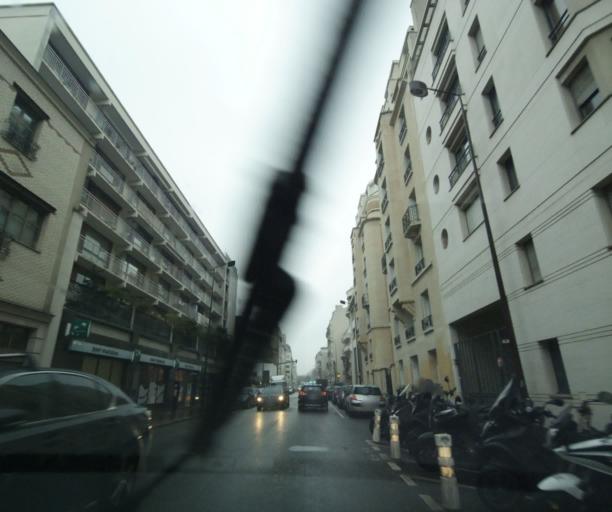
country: FR
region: Ile-de-France
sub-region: Departement des Hauts-de-Seine
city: Levallois-Perret
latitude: 48.8889
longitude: 2.2810
